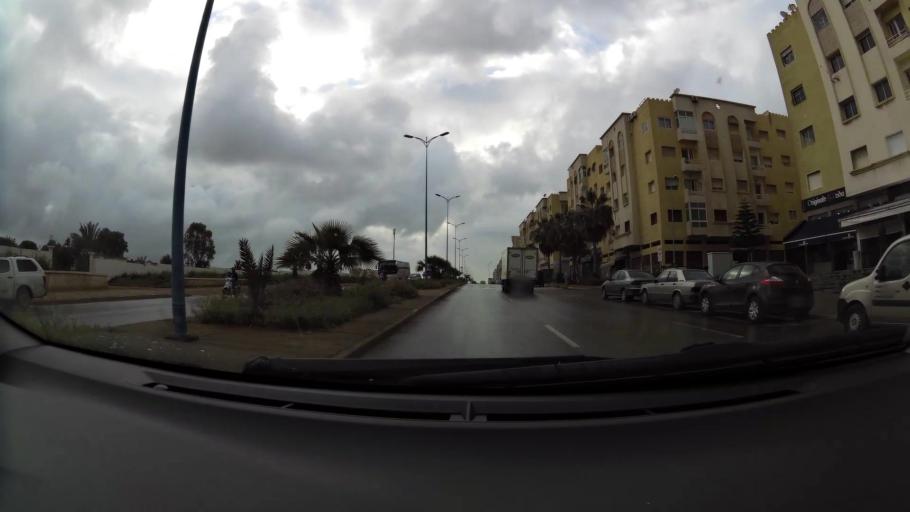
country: MA
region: Grand Casablanca
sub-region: Mohammedia
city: Mohammedia
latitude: 33.6783
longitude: -7.3993
